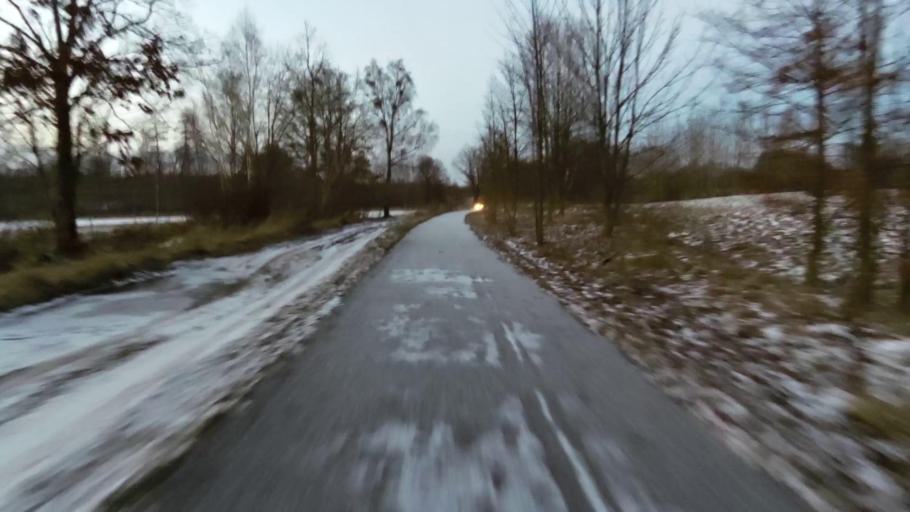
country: PL
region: West Pomeranian Voivodeship
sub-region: Powiat swidwinski
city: Polczyn-Zdroj
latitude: 53.7546
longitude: 16.0568
